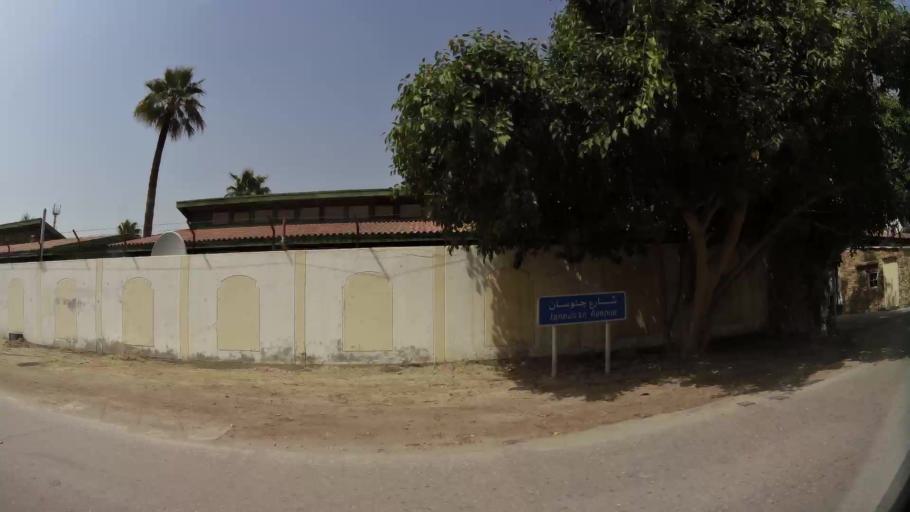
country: BH
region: Manama
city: Jidd Hafs
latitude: 26.2271
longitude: 50.4949
